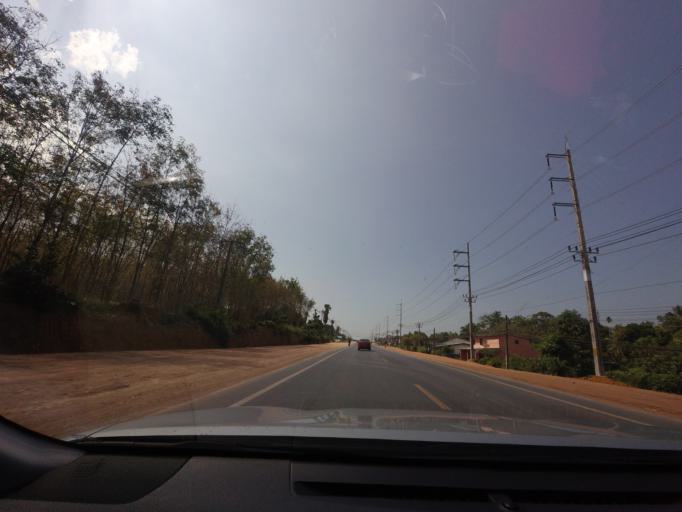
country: TH
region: Phangnga
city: Ban Khao Lak
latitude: 8.6989
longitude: 98.2573
